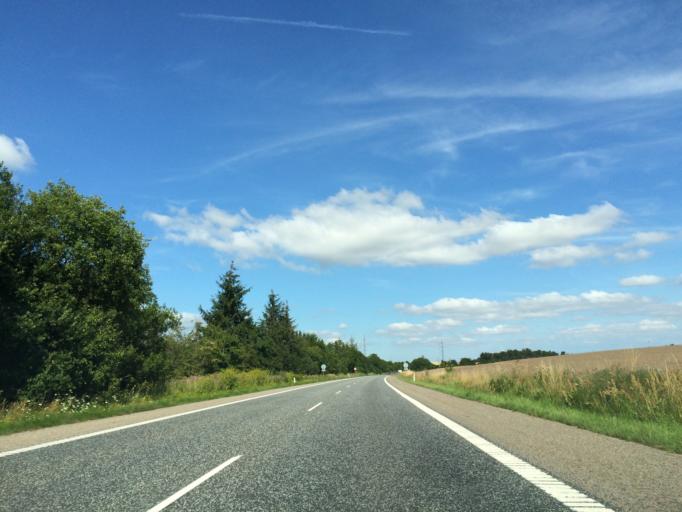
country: DK
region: Central Jutland
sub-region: Syddjurs Kommune
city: Hornslet
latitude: 56.3016
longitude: 10.3457
